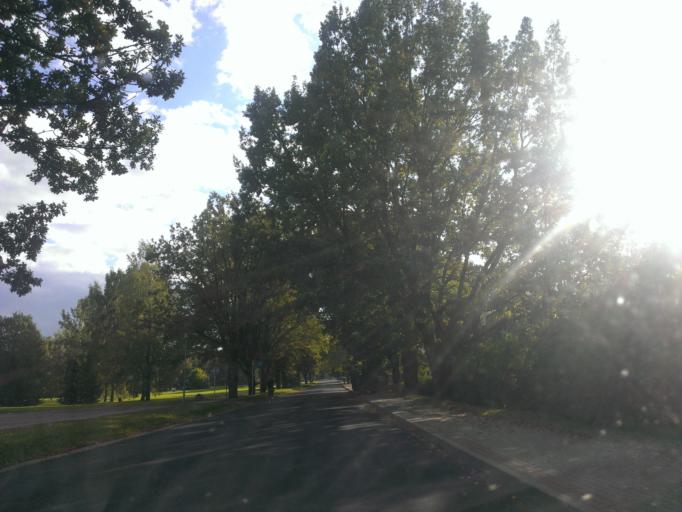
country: LV
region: Sigulda
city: Sigulda
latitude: 57.1612
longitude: 24.8543
